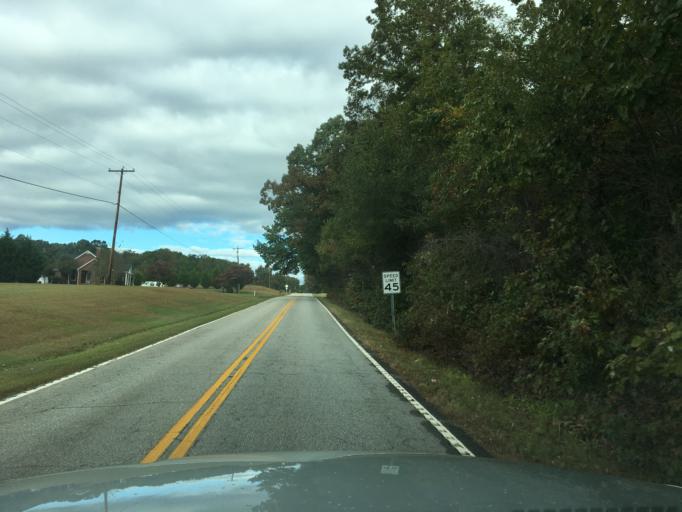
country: US
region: South Carolina
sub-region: Greenville County
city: Tigerville
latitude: 35.0645
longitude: -82.2859
